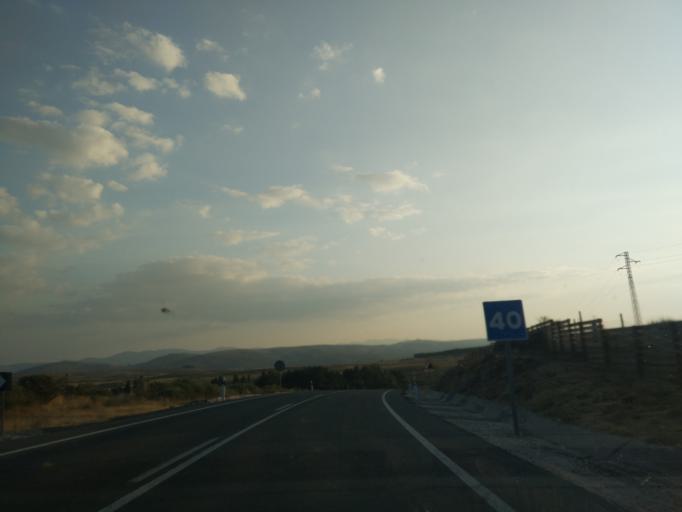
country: ES
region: Castille and Leon
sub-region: Provincia de Avila
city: Cepeda la Mora
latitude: 40.4606
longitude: -5.0246
